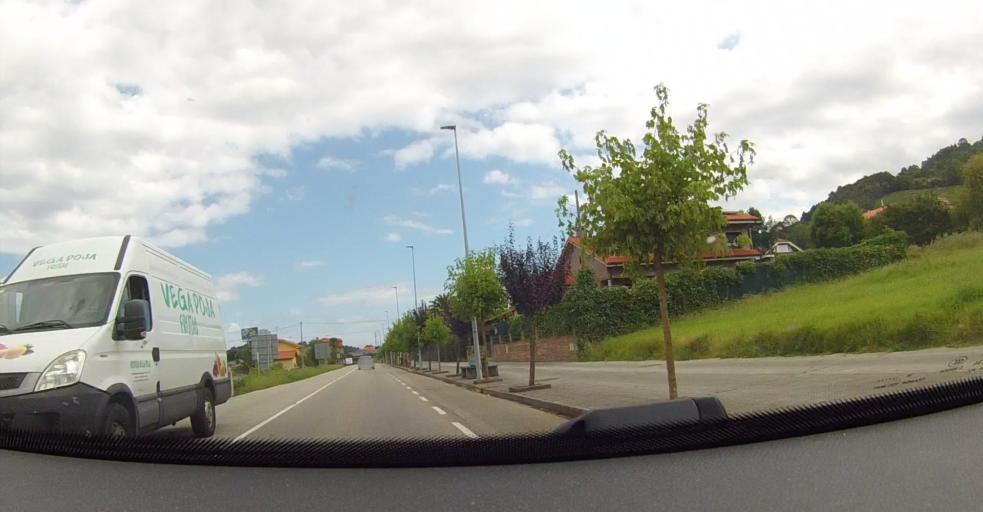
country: ES
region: Asturias
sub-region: Province of Asturias
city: Villaviciosa
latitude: 43.4862
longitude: -5.4282
